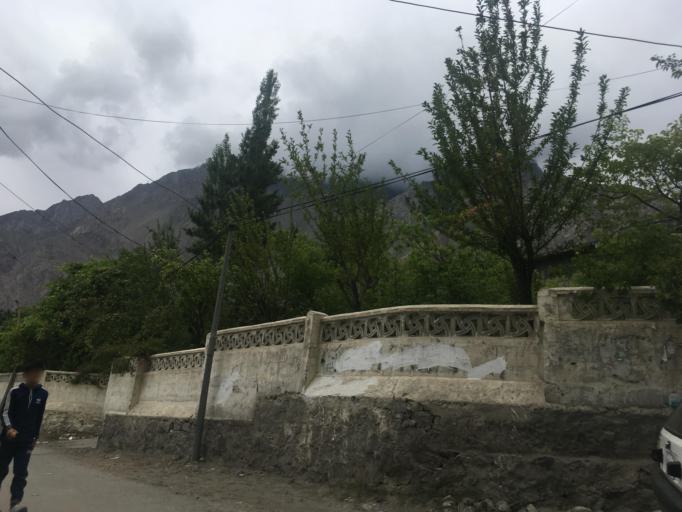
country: PK
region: Gilgit-Baltistan
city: Skardu
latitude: 35.2780
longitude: 75.6376
